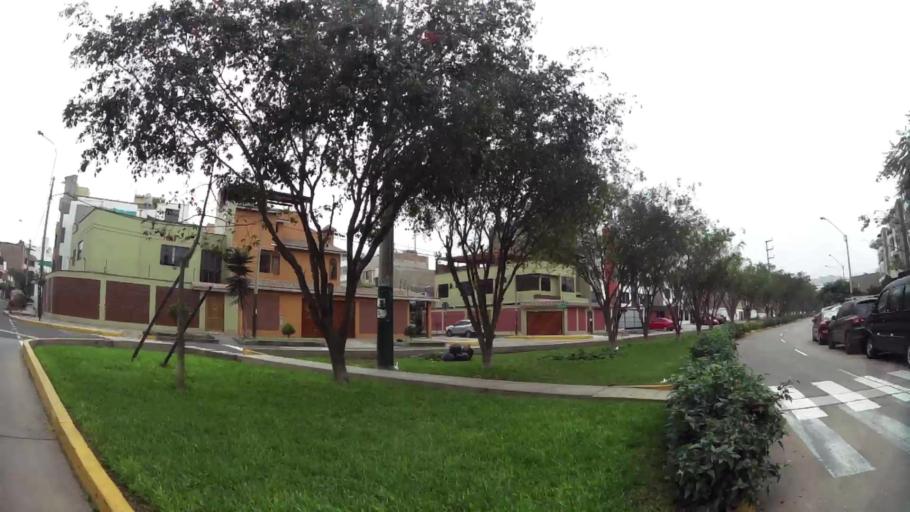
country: PE
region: Lima
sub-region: Lima
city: Surco
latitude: -12.1376
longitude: -76.9855
